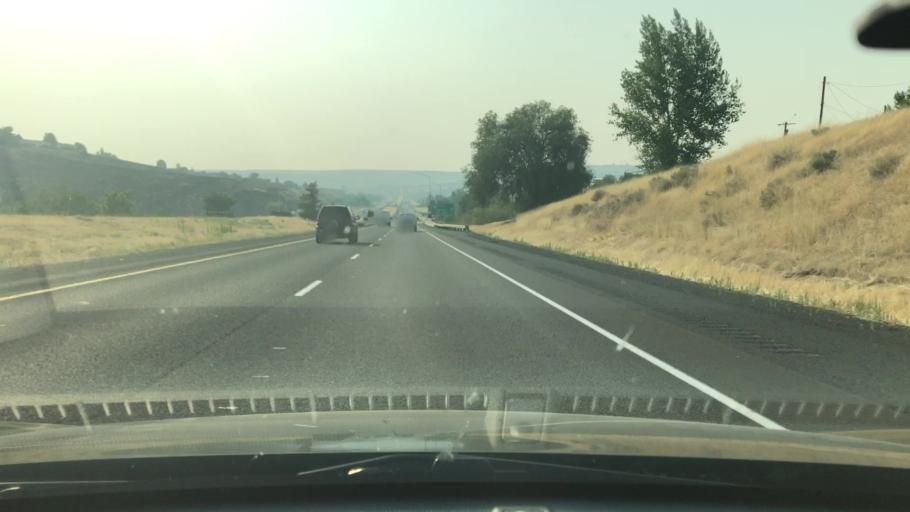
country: US
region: Oregon
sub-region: Umatilla County
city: Pendleton
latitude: 45.6623
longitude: -118.8037
